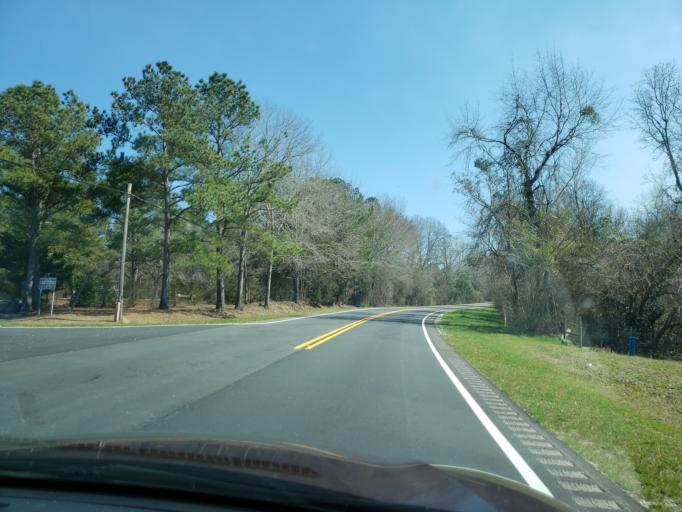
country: US
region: Alabama
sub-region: Macon County
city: Tuskegee
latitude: 32.5782
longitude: -85.6964
